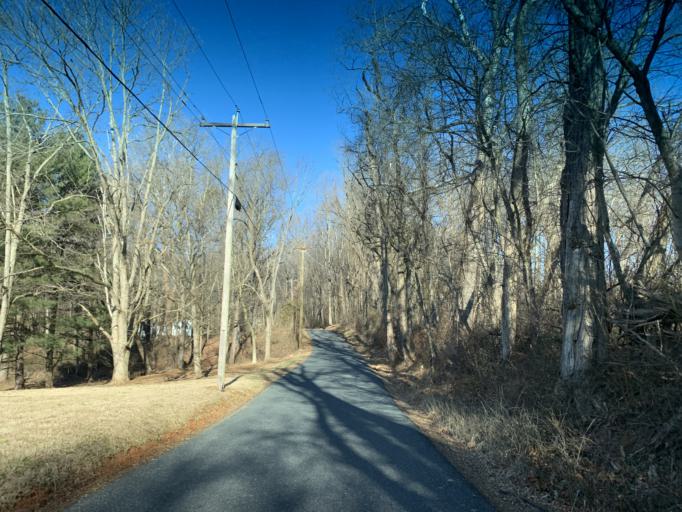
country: US
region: Maryland
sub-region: Harford County
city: South Bel Air
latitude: 39.6211
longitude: -76.2629
